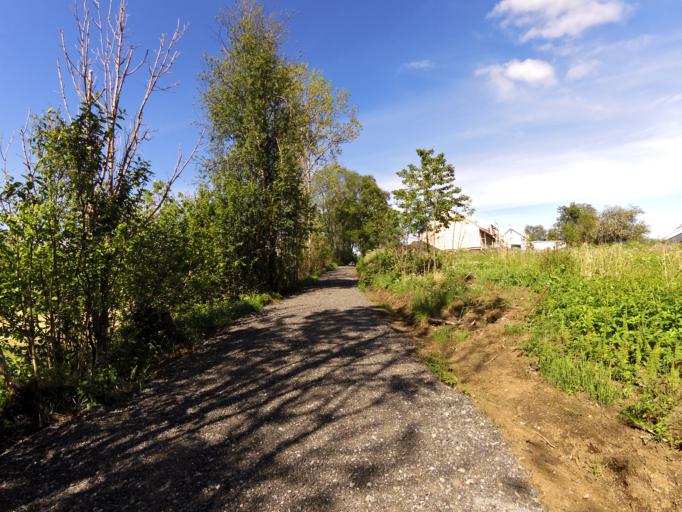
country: NO
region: Hordaland
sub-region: Stord
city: Leirvik
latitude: 59.7878
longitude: 5.4827
